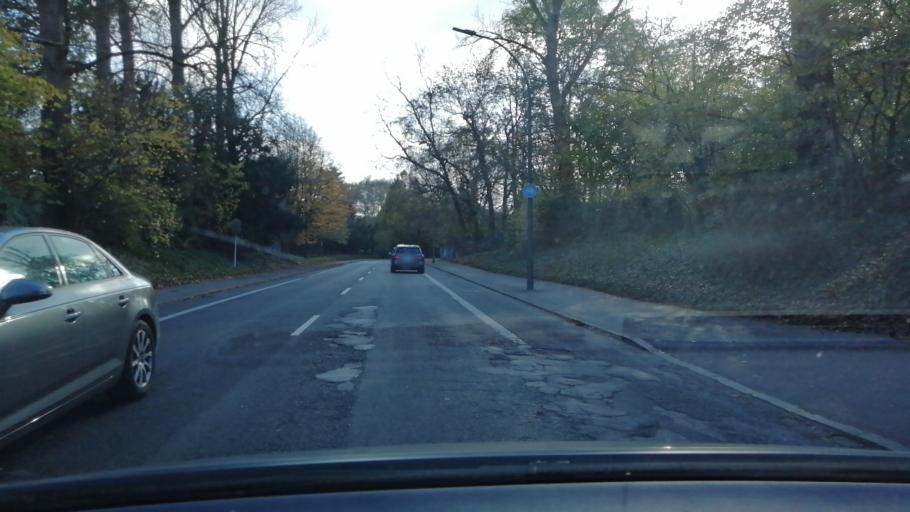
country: DE
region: North Rhine-Westphalia
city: Lanstrop
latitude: 51.5160
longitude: 7.5371
